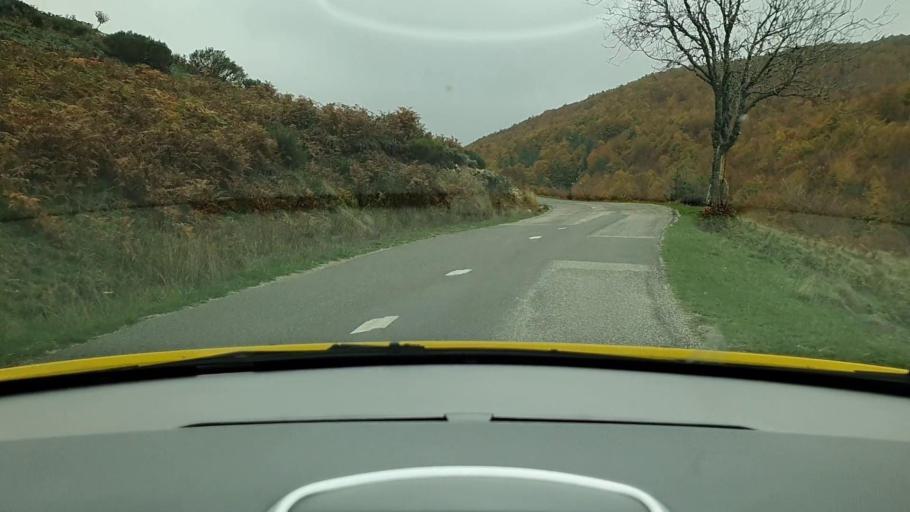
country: FR
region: Languedoc-Roussillon
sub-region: Departement de la Lozere
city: Meyrueis
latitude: 44.0765
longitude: 3.5058
